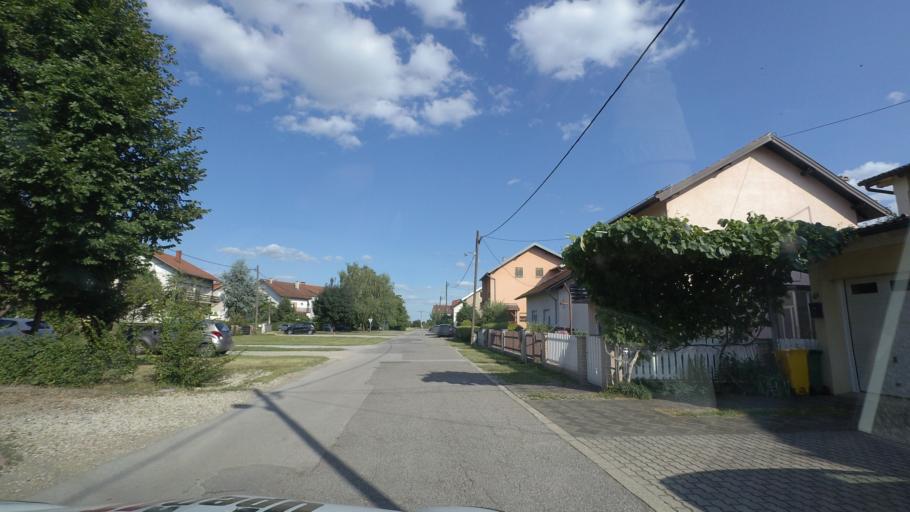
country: HR
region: Zagrebacka
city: Gradici
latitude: 45.7094
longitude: 16.0563
